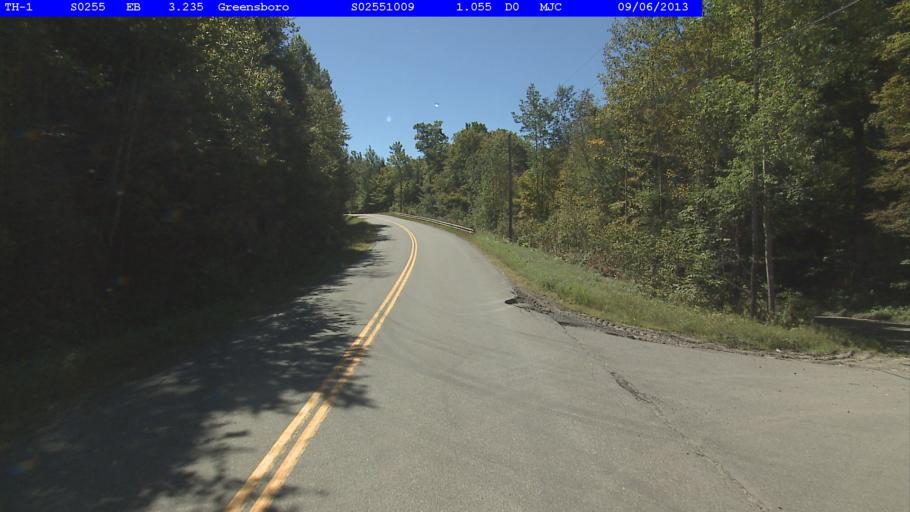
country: US
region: Vermont
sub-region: Caledonia County
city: Hardwick
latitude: 44.6259
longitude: -72.3292
